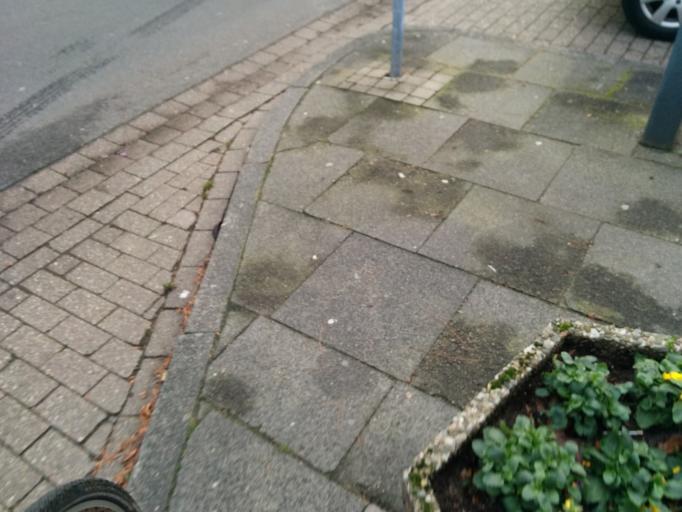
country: DE
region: Lower Saxony
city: Vechta
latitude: 52.7293
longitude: 8.2885
